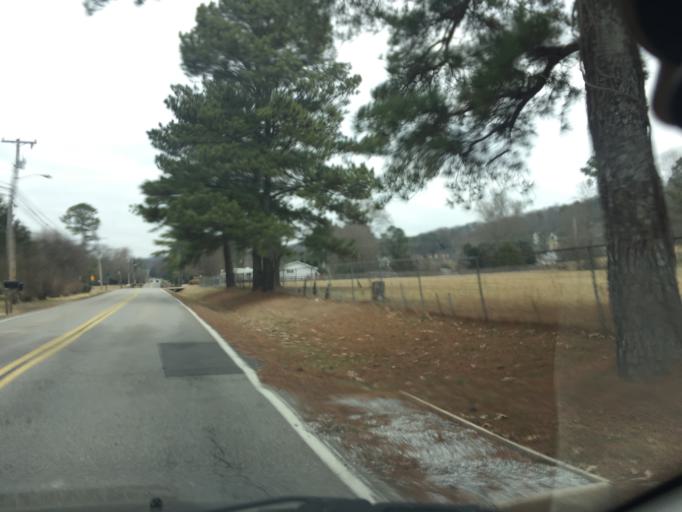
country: US
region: Tennessee
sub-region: Hamilton County
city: East Brainerd
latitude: 35.0049
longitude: -85.1305
